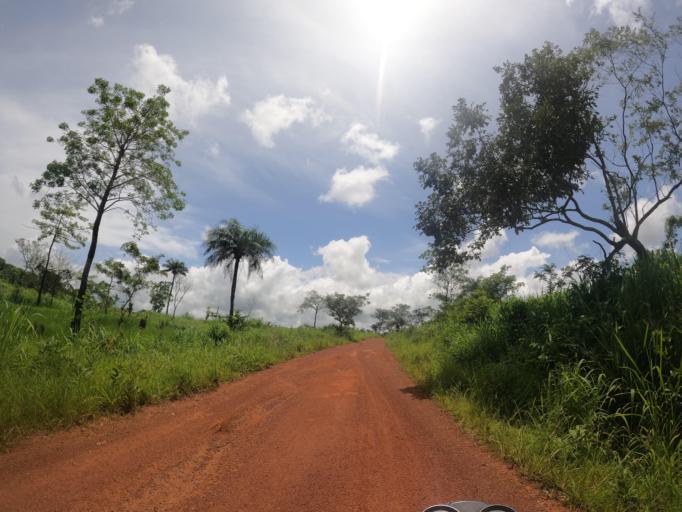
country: SL
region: Northern Province
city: Makeni
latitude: 9.1267
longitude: -12.2499
